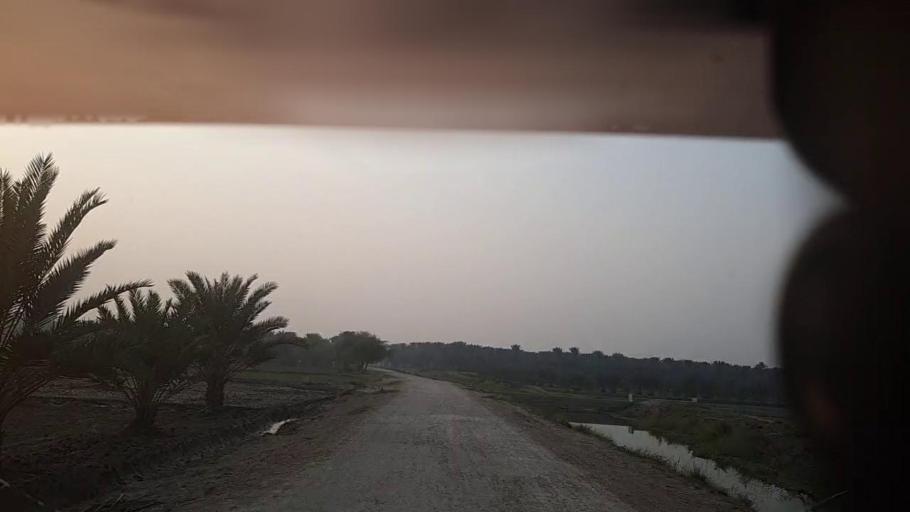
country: PK
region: Sindh
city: Pir jo Goth
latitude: 27.5219
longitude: 68.6445
